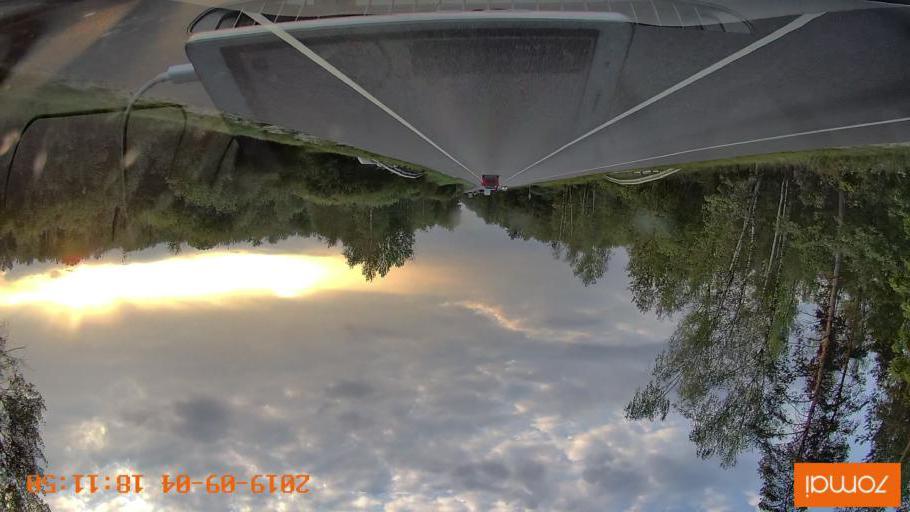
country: RU
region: Moskovskaya
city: Lopatinskiy
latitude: 55.3745
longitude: 38.7501
